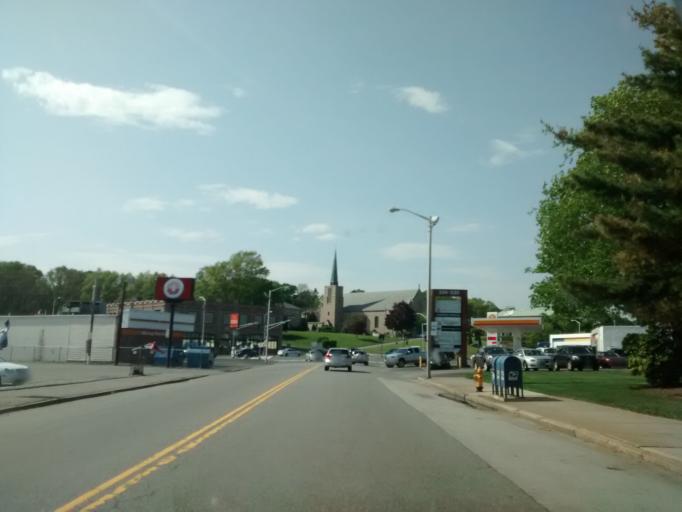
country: US
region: Massachusetts
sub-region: Worcester County
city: Worcester
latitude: 42.2837
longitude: -71.8071
